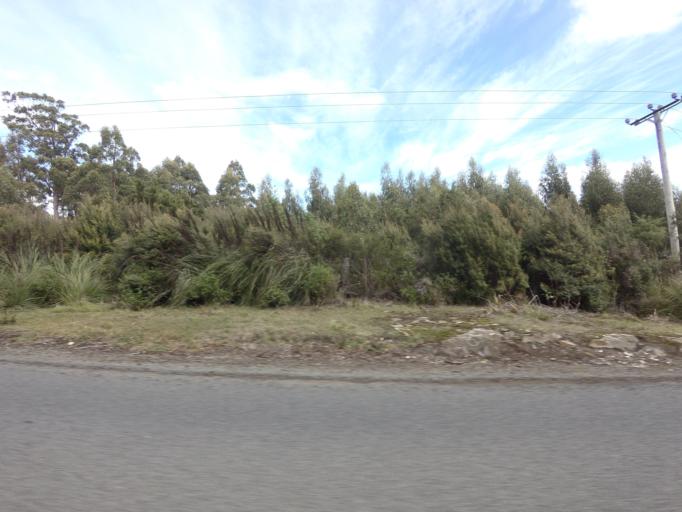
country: AU
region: Tasmania
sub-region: Clarence
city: Sandford
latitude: -43.1377
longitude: 147.8141
